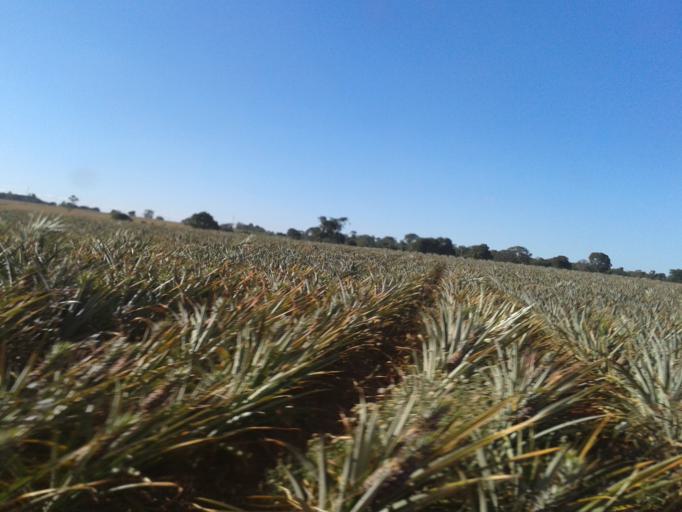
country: BR
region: Minas Gerais
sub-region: Centralina
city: Centralina
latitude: -18.7541
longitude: -49.1009
